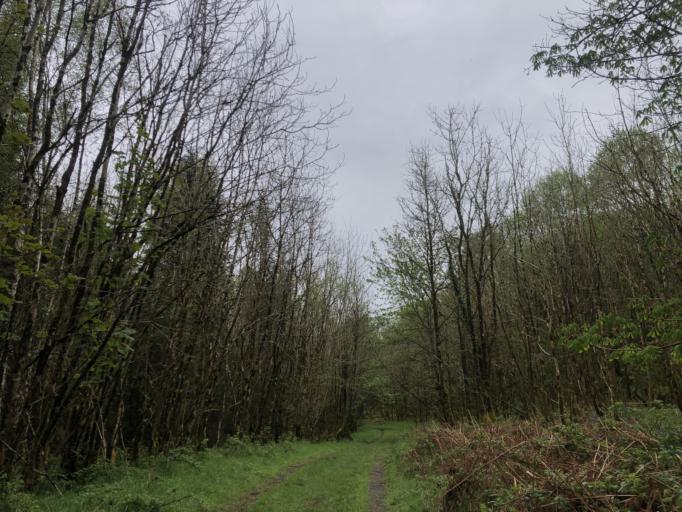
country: IE
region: Connaught
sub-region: County Leitrim
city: Carrick-on-Shannon
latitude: 53.9844
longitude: -8.1870
